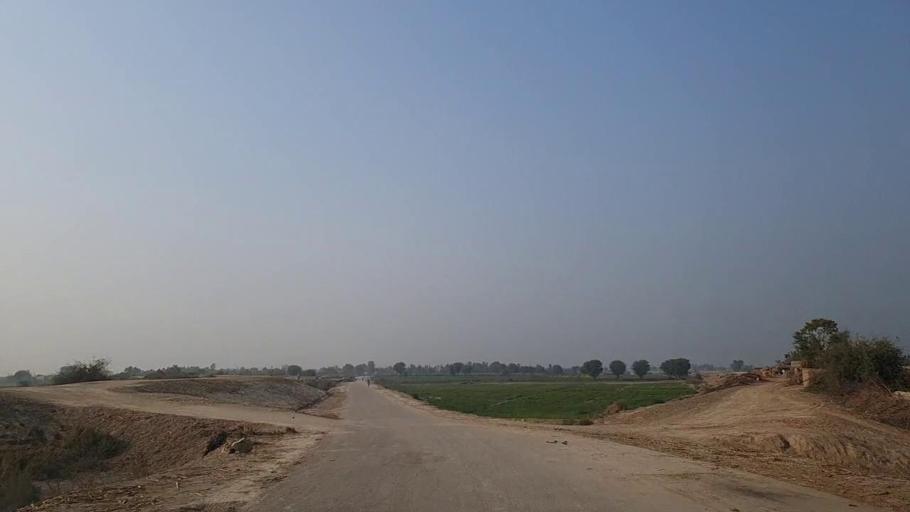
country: PK
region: Sindh
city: Sann
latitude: 26.1187
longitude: 68.1499
